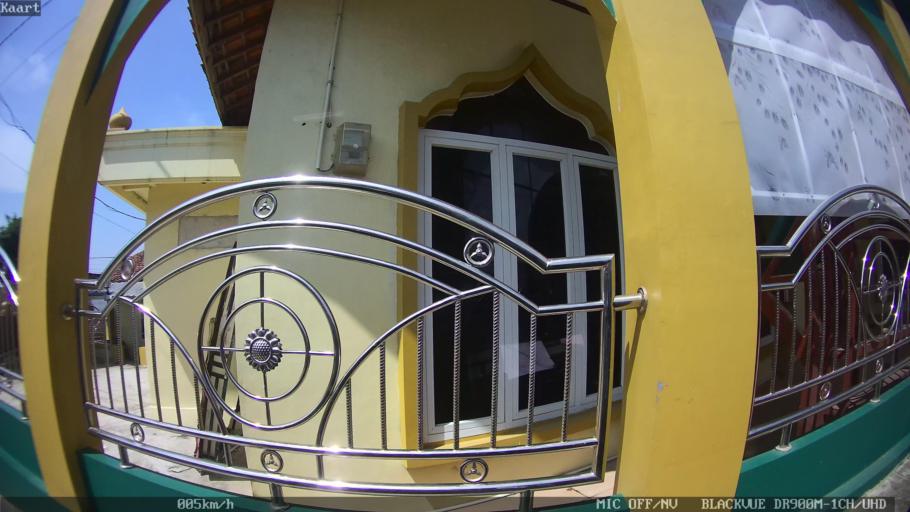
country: ID
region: Lampung
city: Kedaton
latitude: -5.3677
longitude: 105.2495
